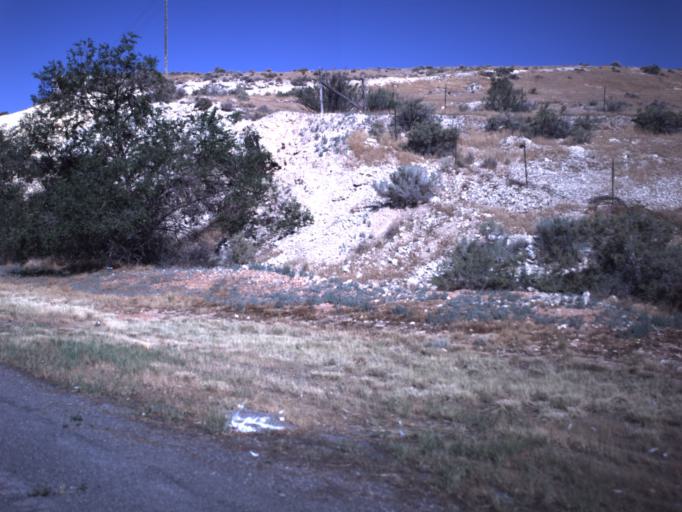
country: US
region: Utah
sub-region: Sanpete County
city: Gunnison
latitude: 39.1597
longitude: -111.7509
